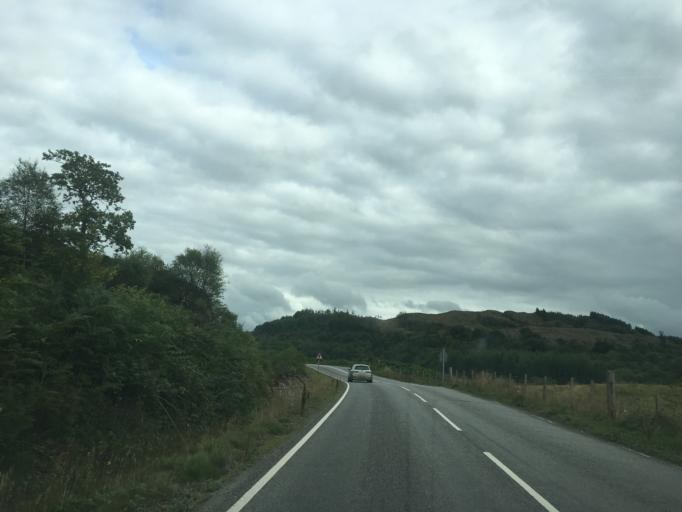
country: GB
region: Scotland
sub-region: Argyll and Bute
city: Oban
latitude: 56.3226
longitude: -5.4981
